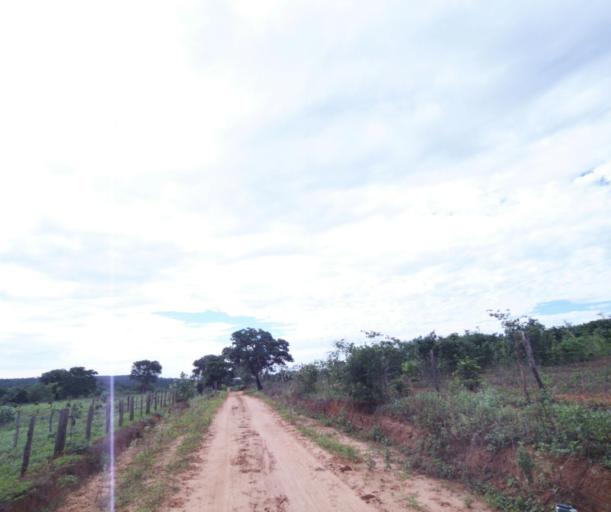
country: BR
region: Bahia
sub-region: Carinhanha
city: Carinhanha
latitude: -14.2108
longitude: -44.4539
